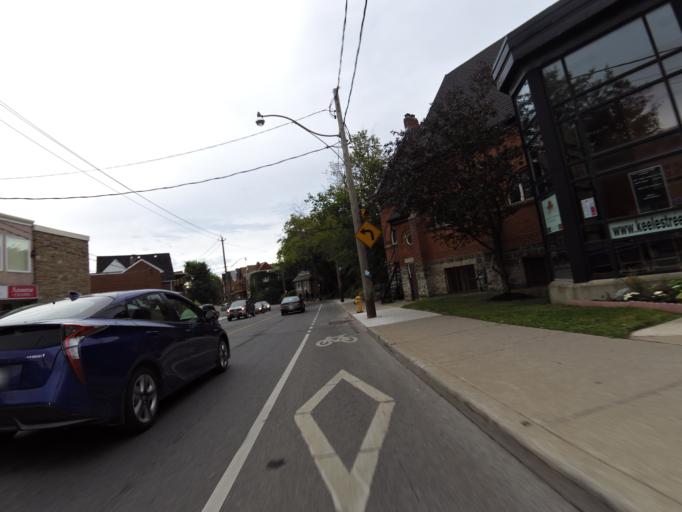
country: CA
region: Ontario
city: Toronto
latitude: 43.6635
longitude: -79.4634
